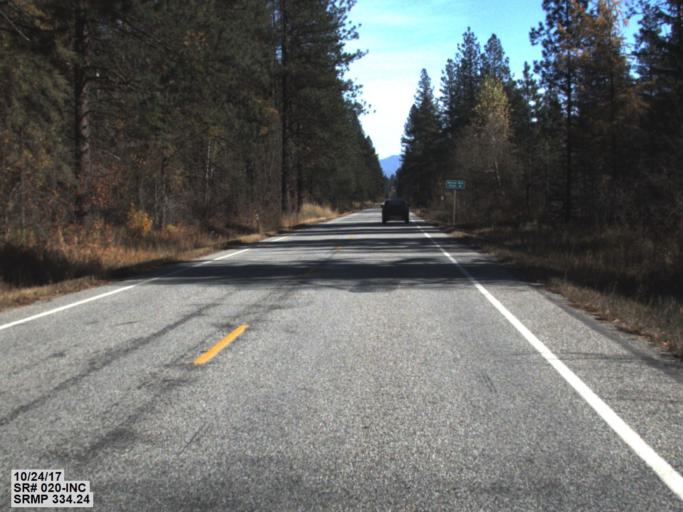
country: US
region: Washington
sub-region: Stevens County
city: Kettle Falls
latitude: 48.5799
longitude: -118.2444
